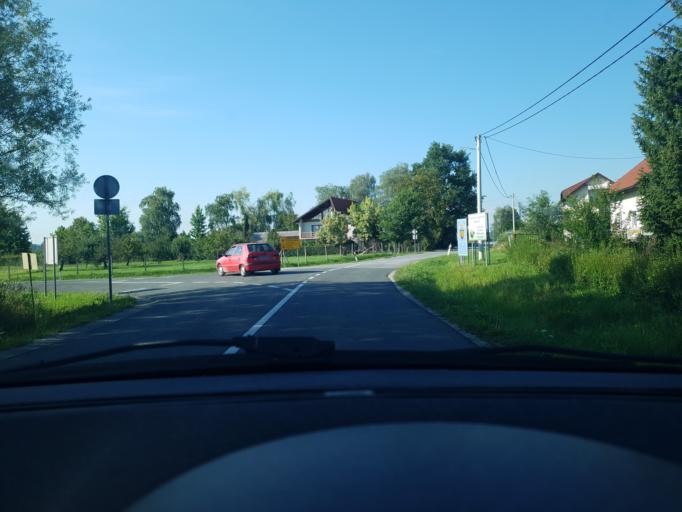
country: HR
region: Zagrebacka
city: Jakovlje
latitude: 45.9739
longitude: 15.8576
